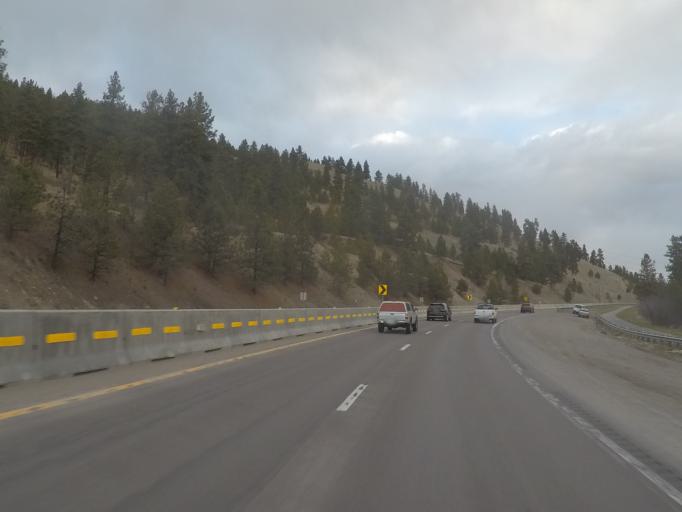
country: US
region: Montana
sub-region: Missoula County
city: Lolo
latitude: 46.7902
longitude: -114.1026
